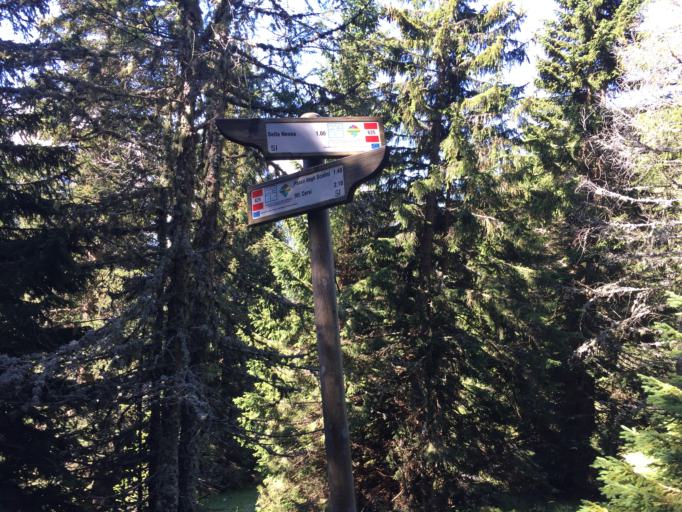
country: SI
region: Bovec
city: Bovec
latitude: 46.4023
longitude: 13.4806
